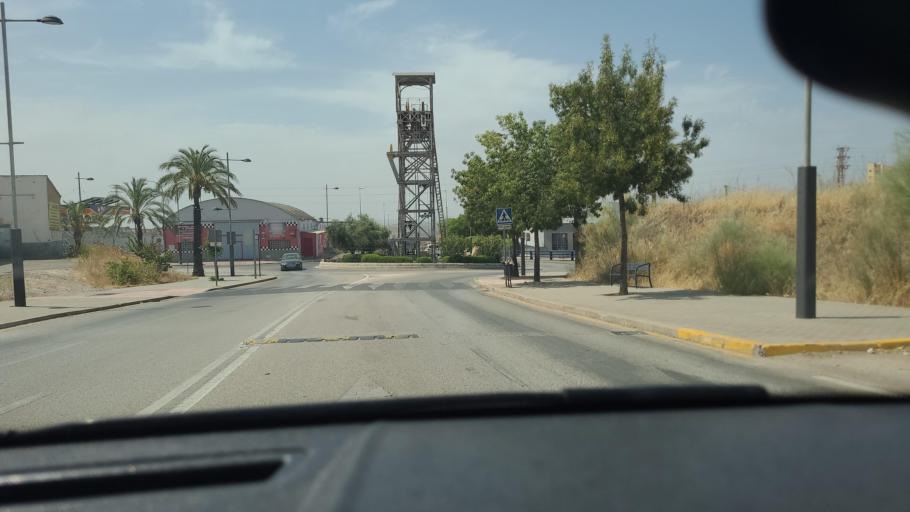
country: ES
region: Andalusia
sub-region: Provincia de Jaen
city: Linares
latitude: 38.0855
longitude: -3.6395
